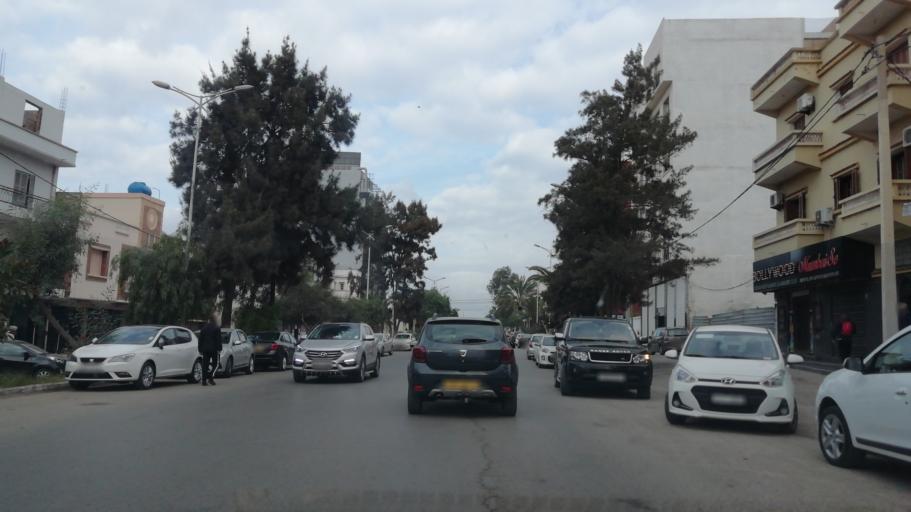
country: DZ
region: Oran
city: Oran
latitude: 35.7107
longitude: -0.6115
